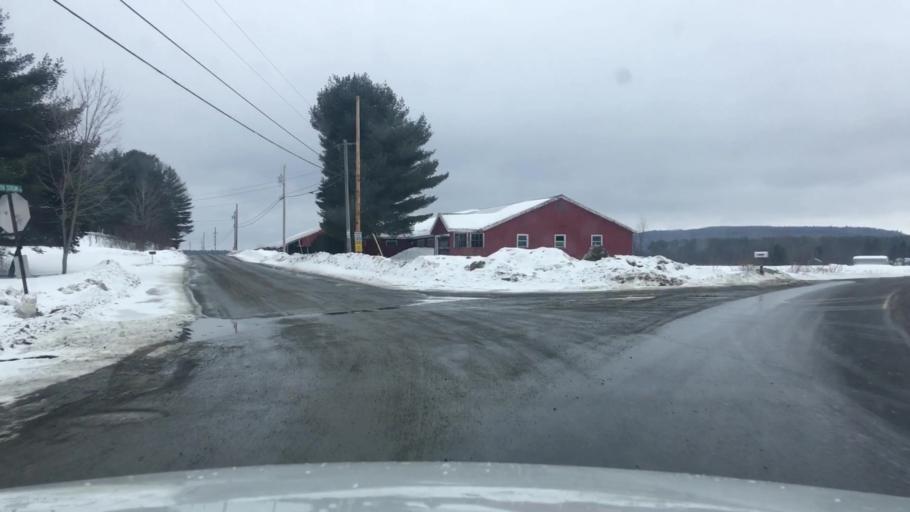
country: US
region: Maine
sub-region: Somerset County
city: Norridgewock
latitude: 44.7068
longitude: -69.7913
